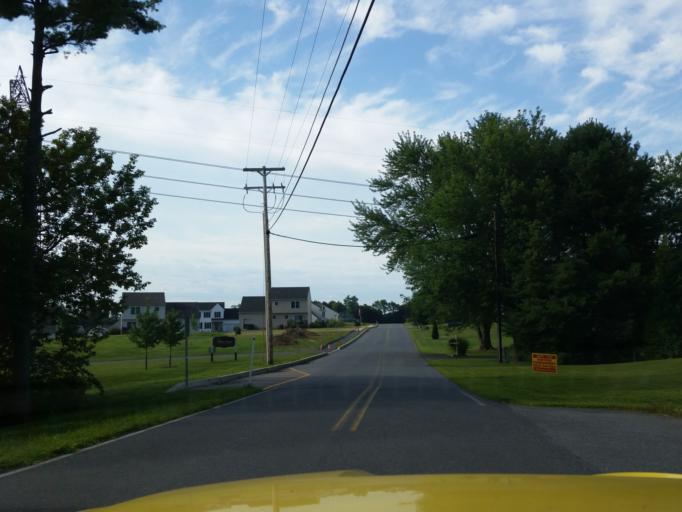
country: US
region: Pennsylvania
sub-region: Lebanon County
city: Jonestown
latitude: 40.4231
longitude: -76.4726
